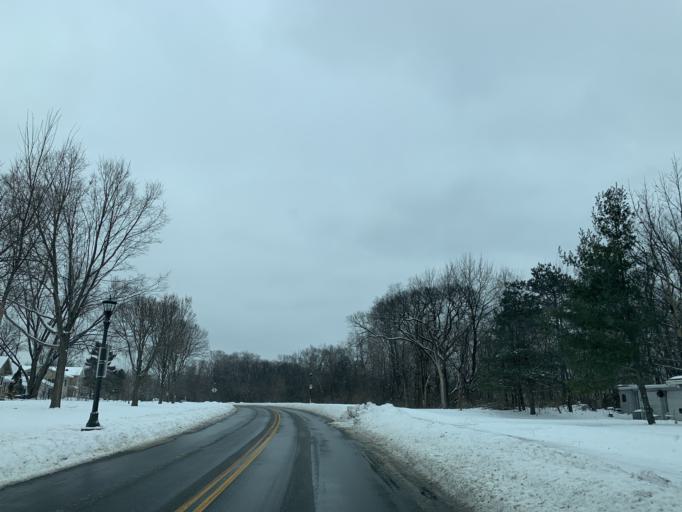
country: US
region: Minnesota
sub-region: Ramsey County
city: Roseville
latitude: 44.9849
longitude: -93.1157
